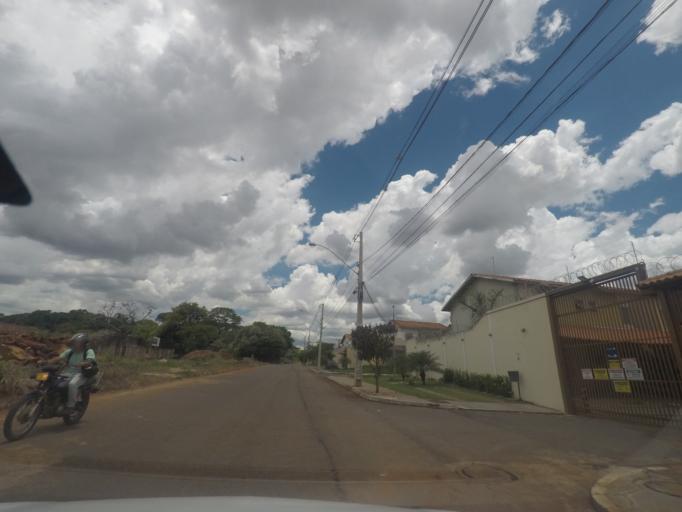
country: BR
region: Goias
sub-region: Goiania
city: Goiania
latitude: -16.7123
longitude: -49.3439
